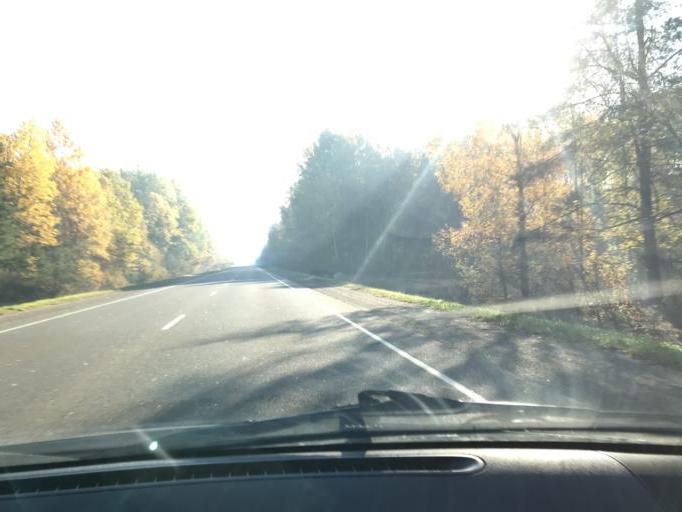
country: BY
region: Brest
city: Horad Luninyets
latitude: 52.2934
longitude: 26.7597
